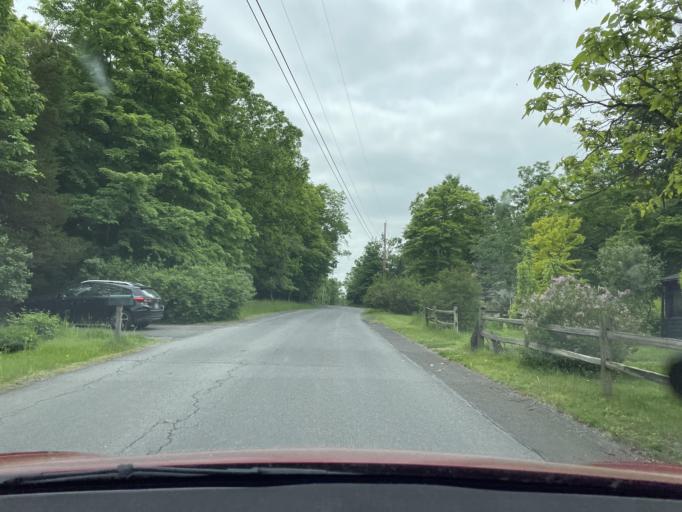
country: US
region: New York
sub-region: Ulster County
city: Zena
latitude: 41.9878
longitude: -74.0611
